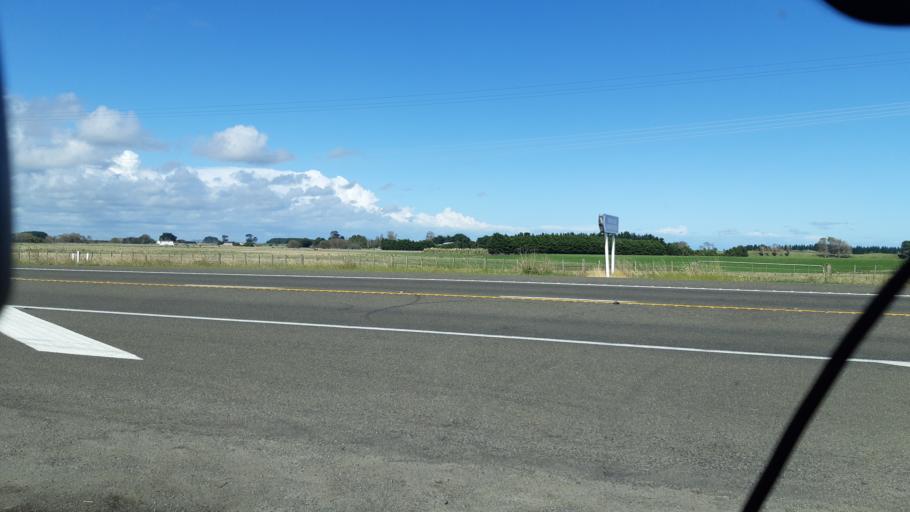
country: NZ
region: Manawatu-Wanganui
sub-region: Wanganui District
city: Wanganui
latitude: -39.9749
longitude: 175.1228
